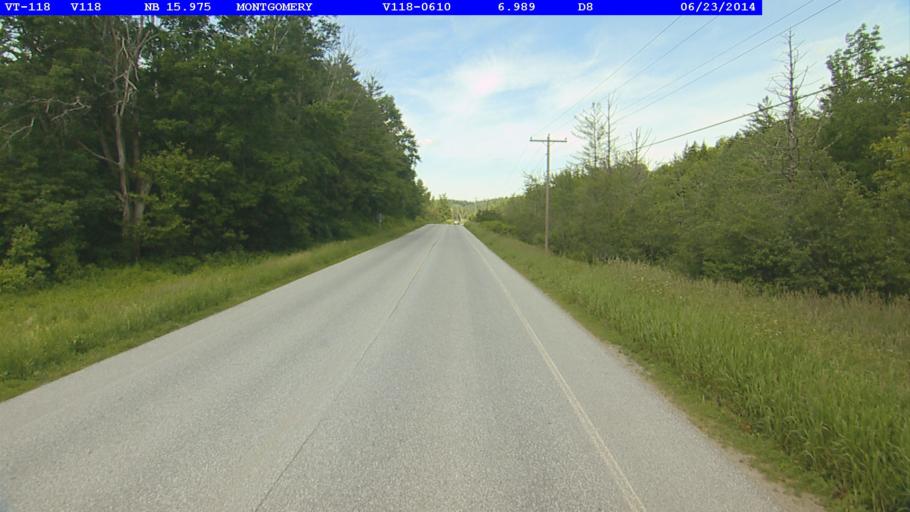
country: US
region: Vermont
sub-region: Franklin County
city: Richford
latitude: 44.8935
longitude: -72.6230
